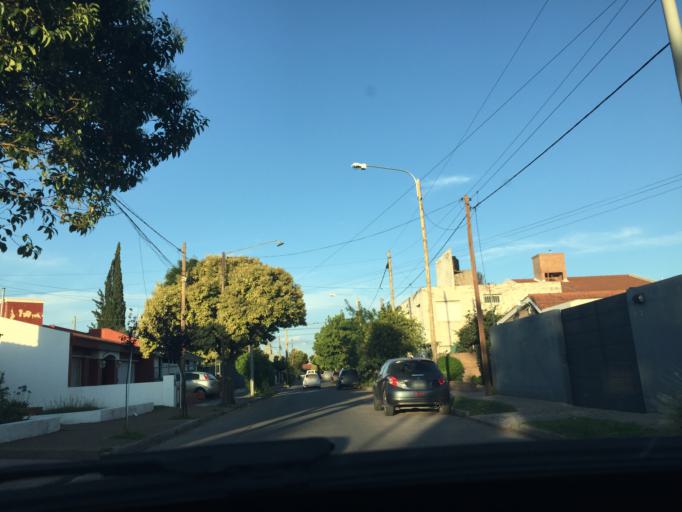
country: AR
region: Cordoba
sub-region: Departamento de Capital
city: Cordoba
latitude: -31.3640
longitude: -64.2293
